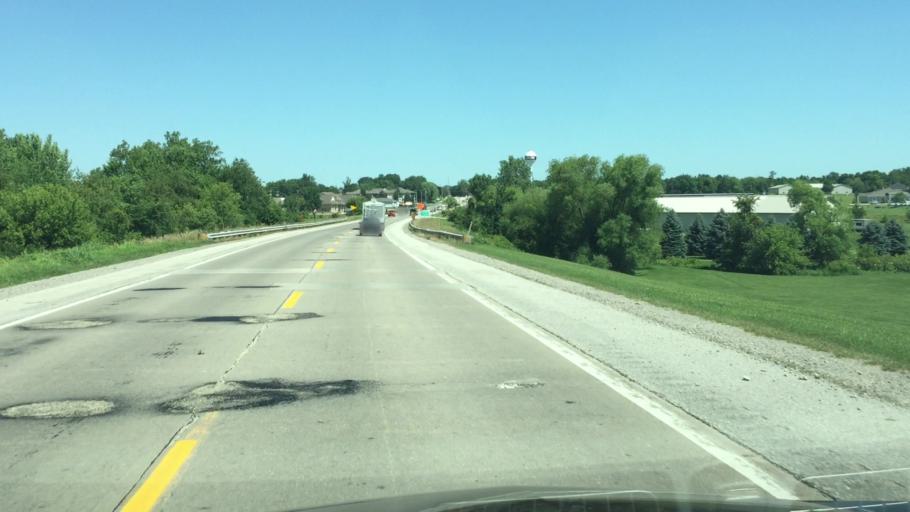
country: US
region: Iowa
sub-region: Johnson County
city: Solon
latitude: 41.7936
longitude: -91.4896
